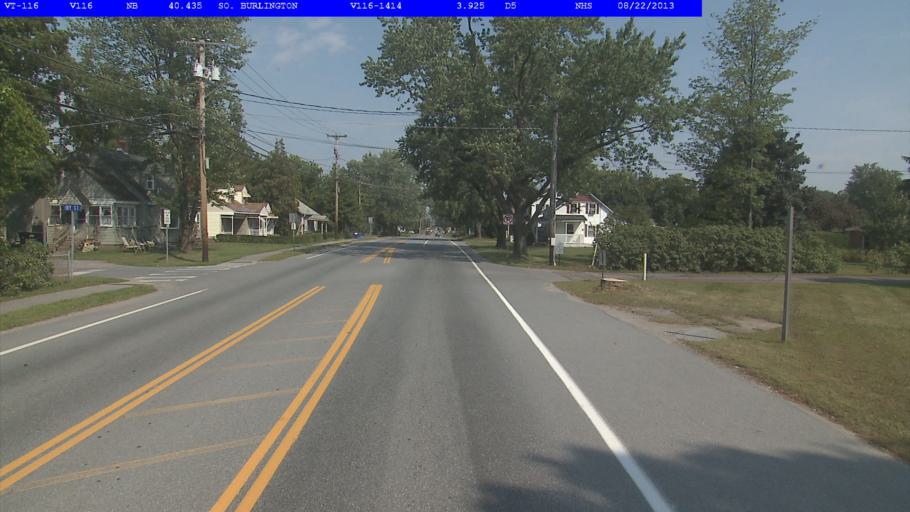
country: US
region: Vermont
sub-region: Chittenden County
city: South Burlington
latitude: 44.4625
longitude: -73.1704
